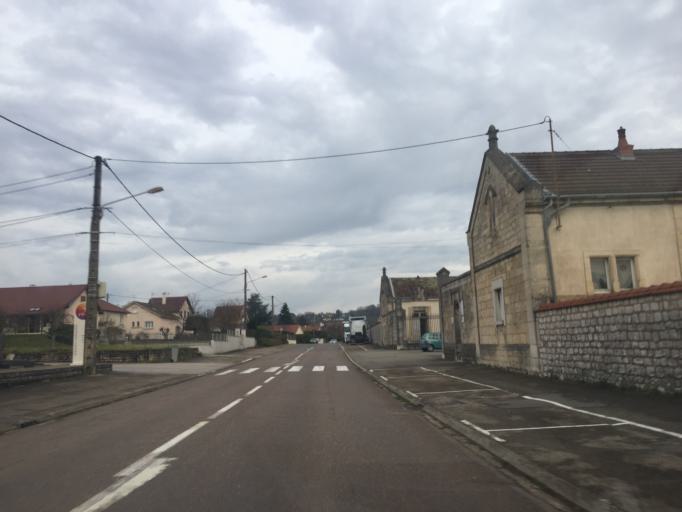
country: FR
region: Franche-Comte
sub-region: Departement du Jura
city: Dole
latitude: 47.1019
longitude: 5.4899
